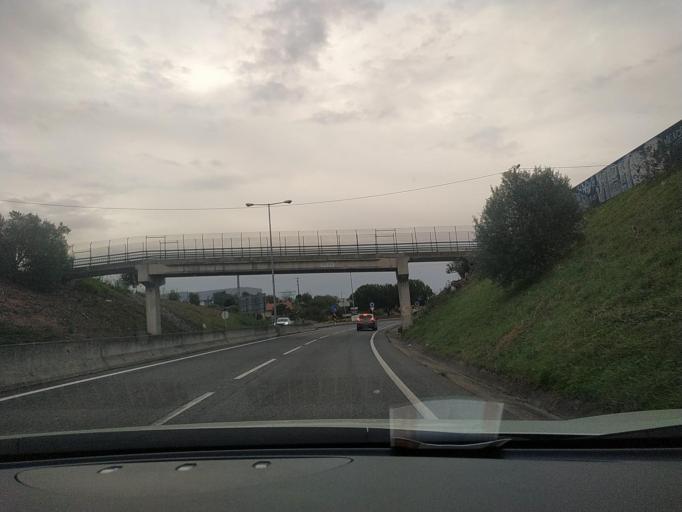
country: PT
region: Lisbon
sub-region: Loures
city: Santo Antao do Tojal
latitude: 38.8610
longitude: -9.1244
